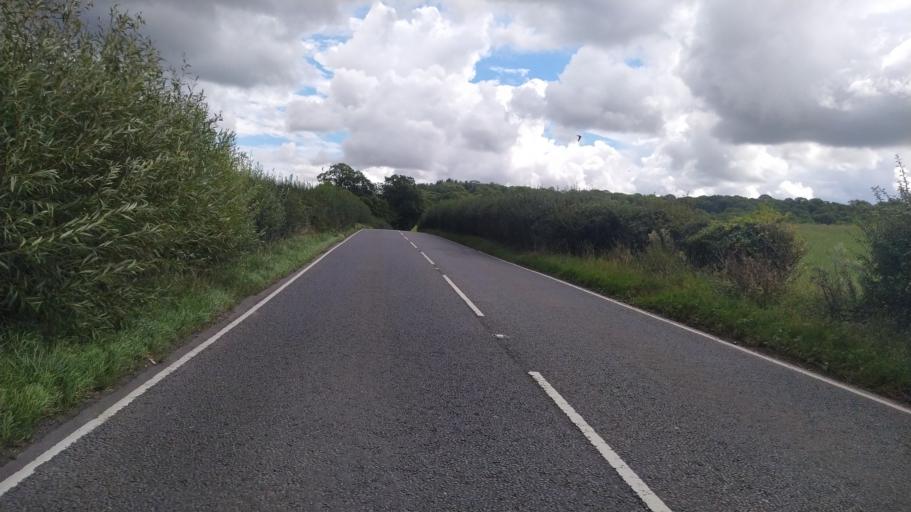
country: GB
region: England
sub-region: Dorset
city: Sturminster Newton
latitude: 50.9203
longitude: -2.2998
